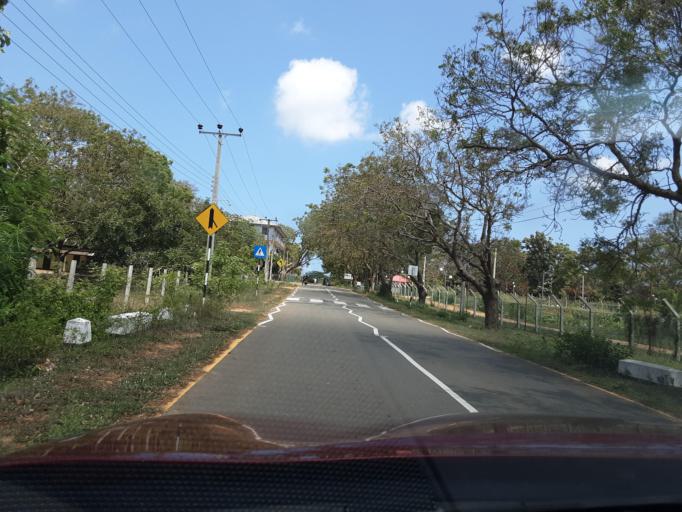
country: LK
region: Southern
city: Tangalla
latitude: 6.2083
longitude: 81.2062
